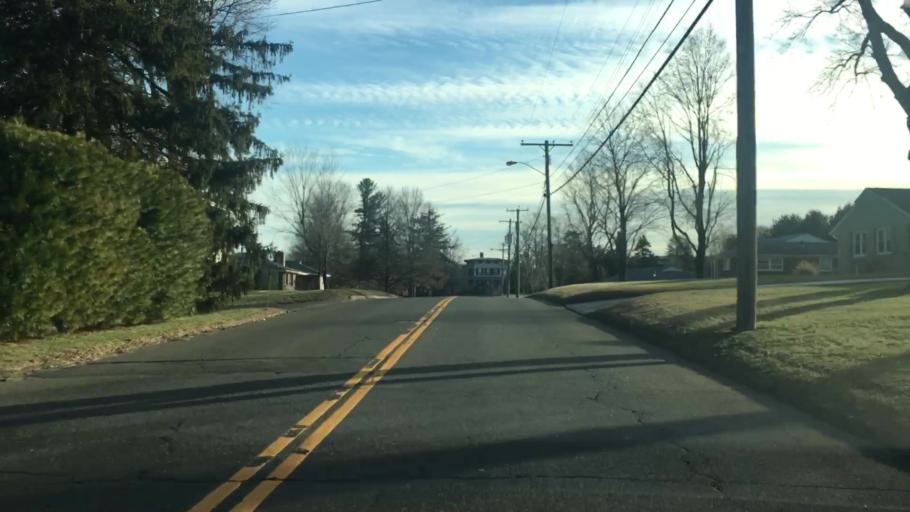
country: US
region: Connecticut
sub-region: Middlesex County
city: Middletown
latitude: 41.5340
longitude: -72.6498
